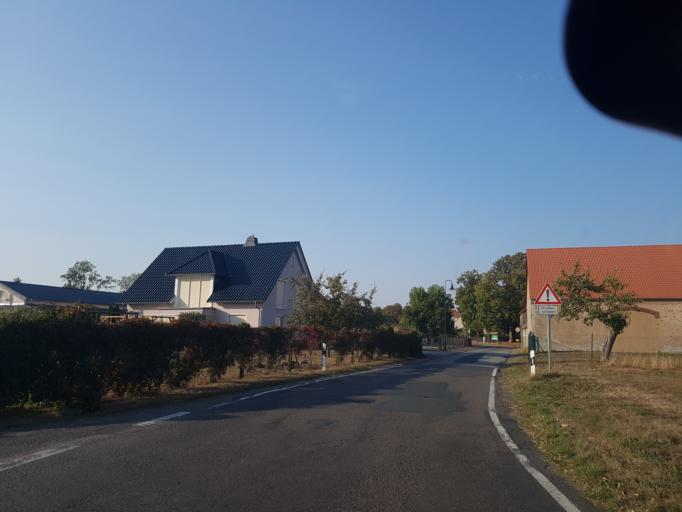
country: DE
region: Saxony
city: Strehla
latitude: 51.3364
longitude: 13.1943
